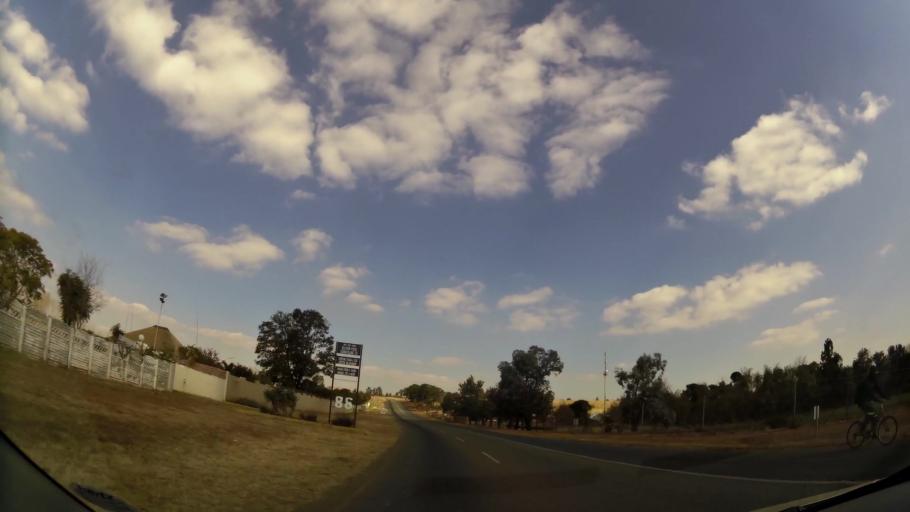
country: ZA
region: Gauteng
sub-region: West Rand District Municipality
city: Krugersdorp
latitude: -26.0513
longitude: 27.7540
